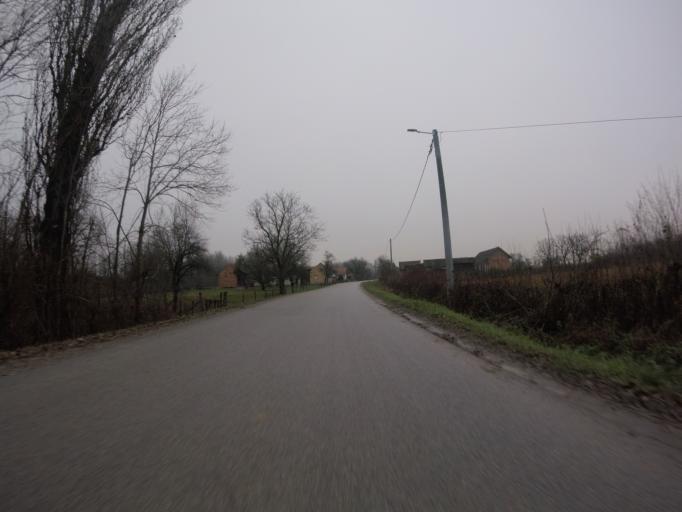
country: HR
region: Sisacko-Moslavacka
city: Lekenik
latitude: 45.6312
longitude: 16.3090
